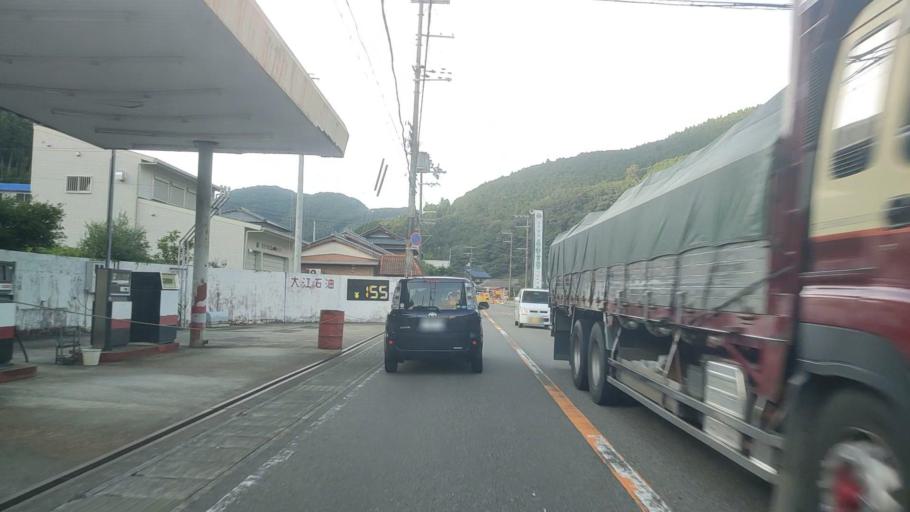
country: JP
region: Wakayama
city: Tanabe
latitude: 33.7929
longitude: 135.5176
